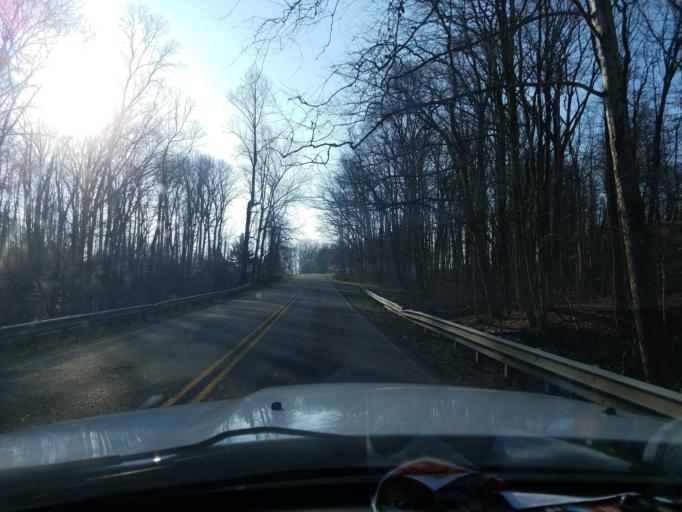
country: US
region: Indiana
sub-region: Owen County
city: Spencer
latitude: 39.3434
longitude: -86.9077
